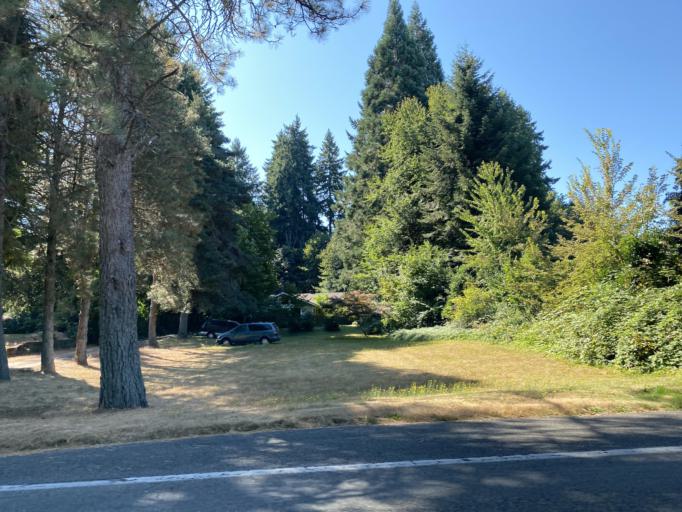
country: US
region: Washington
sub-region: Thurston County
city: Olympia
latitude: 47.0295
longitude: -122.8813
